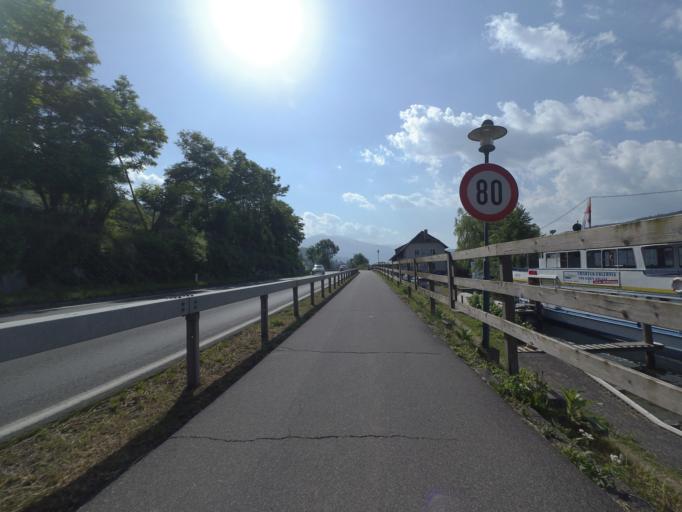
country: AT
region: Carinthia
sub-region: Politischer Bezirk Spittal an der Drau
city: Millstatt
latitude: 46.8093
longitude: 13.5539
